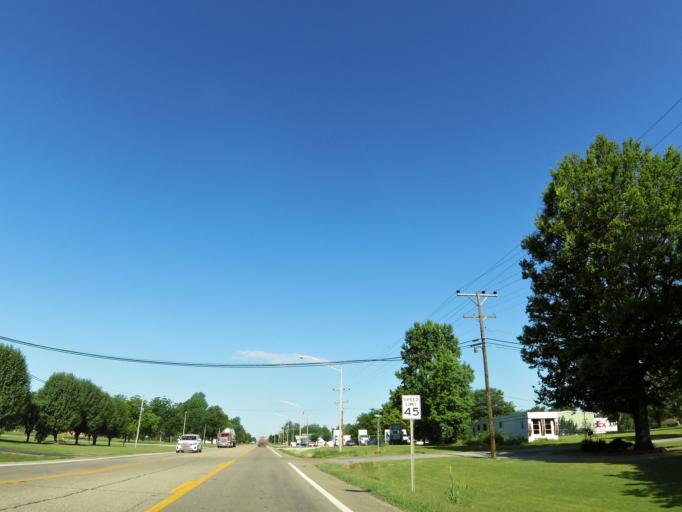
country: US
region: Arkansas
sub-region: Clay County
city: Corning
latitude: 36.4114
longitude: -90.5994
